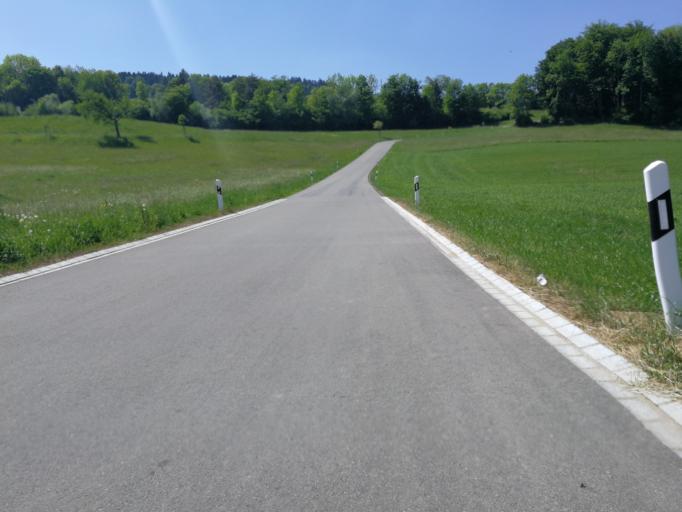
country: CH
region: Zurich
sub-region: Bezirk Uster
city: Hinteregg
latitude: 47.3189
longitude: 8.6695
